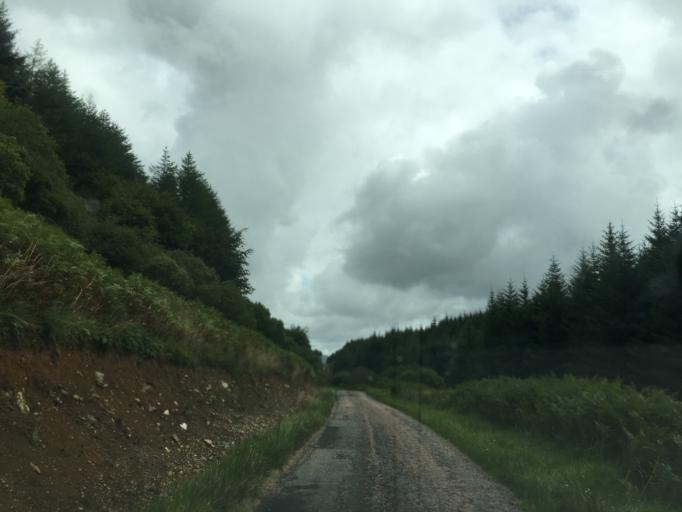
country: GB
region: Scotland
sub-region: Argyll and Bute
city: Oban
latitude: 56.2503
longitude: -5.4185
